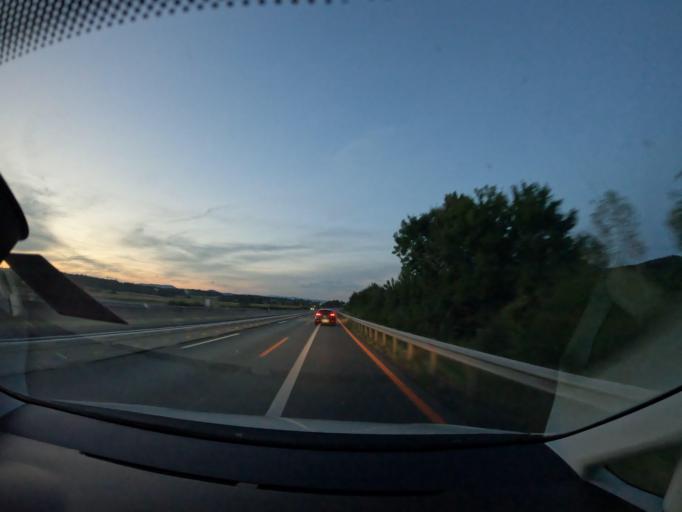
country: AT
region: Styria
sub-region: Politischer Bezirk Hartberg-Fuerstenfeld
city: Sebersdorf
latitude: 47.2095
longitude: 15.9861
